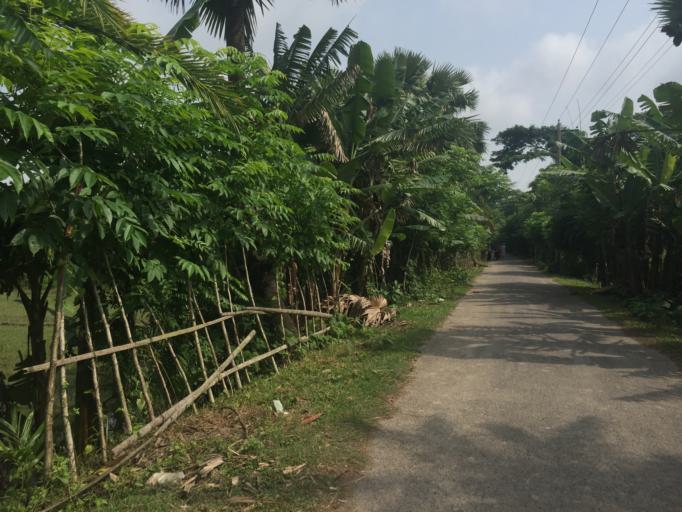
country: BD
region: Barisal
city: Mathba
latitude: 22.2385
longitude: 89.9150
